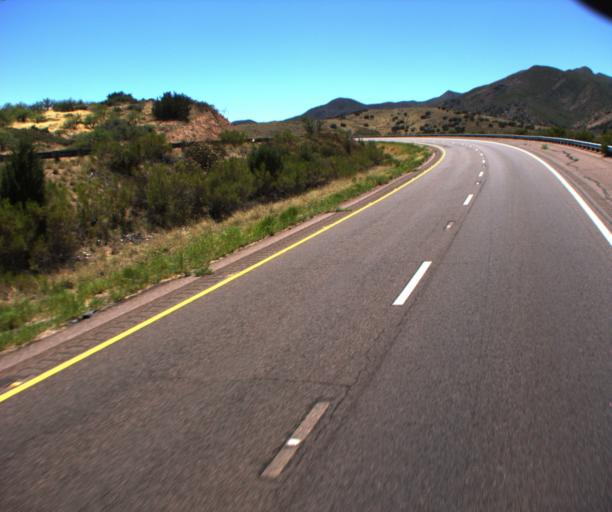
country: US
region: Arizona
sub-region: Gila County
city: Tonto Basin
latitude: 33.9968
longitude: -111.3660
